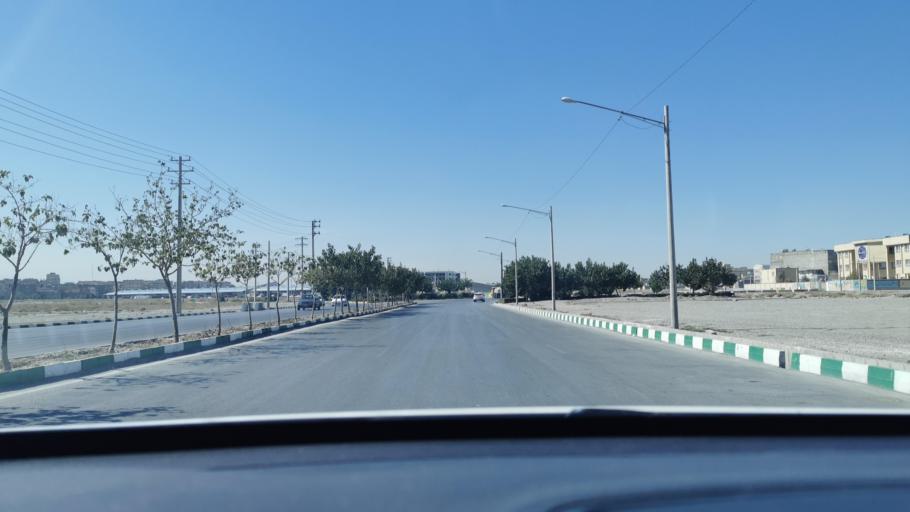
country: IR
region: Razavi Khorasan
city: Mashhad
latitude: 36.3358
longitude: 59.6246
